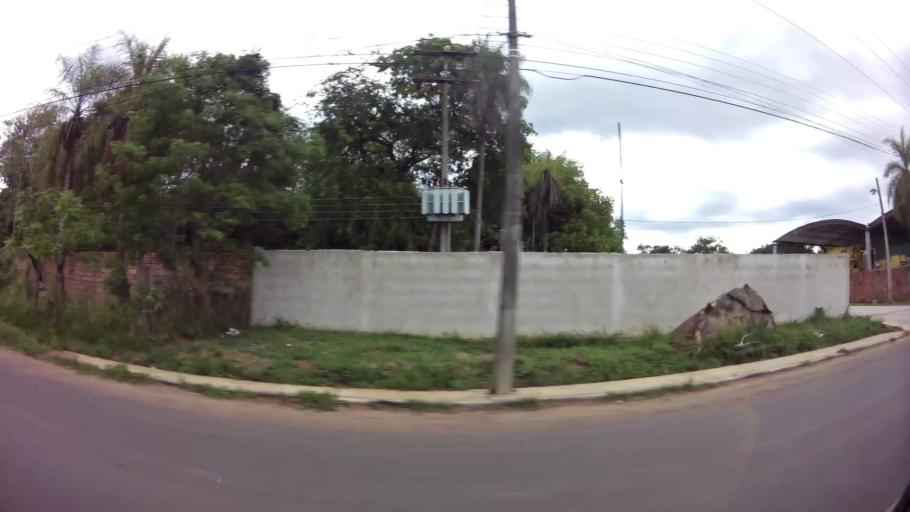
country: PY
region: Central
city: San Lorenzo
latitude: -25.2882
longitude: -57.4901
